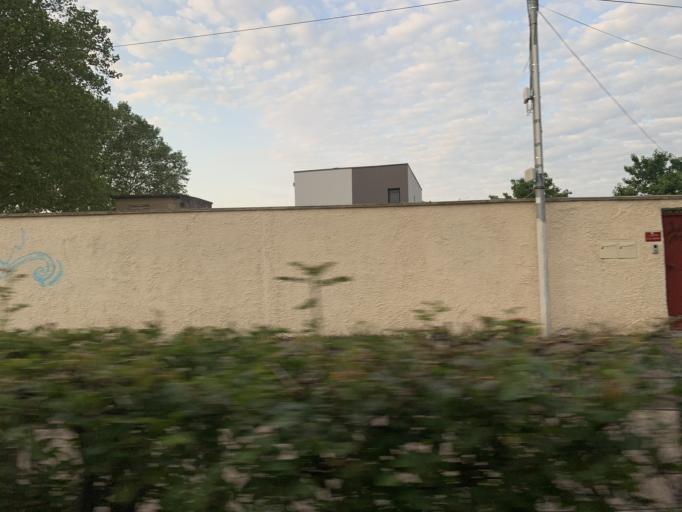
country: FR
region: Rhone-Alpes
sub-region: Departement du Rhone
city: Villeurbanne
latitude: 45.7528
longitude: 4.8795
